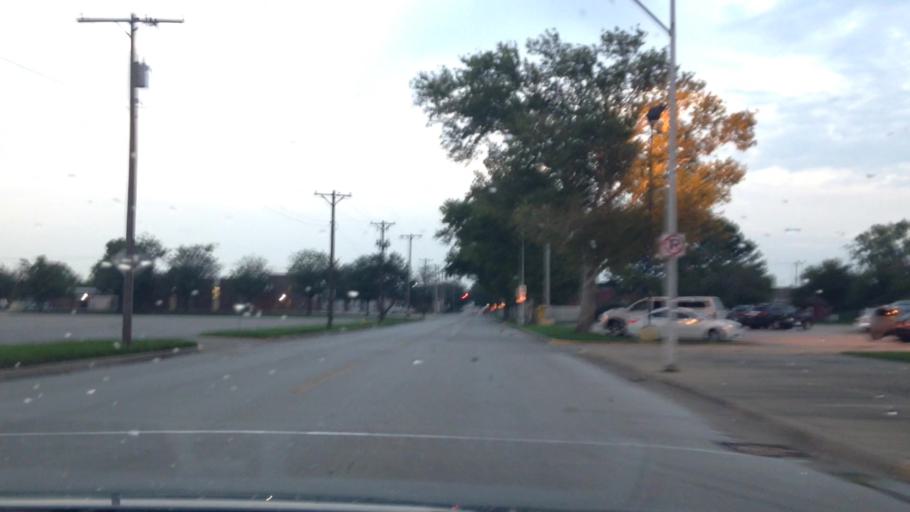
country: US
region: Missouri
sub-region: Clay County
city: North Kansas City
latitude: 39.1402
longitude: -94.5746
